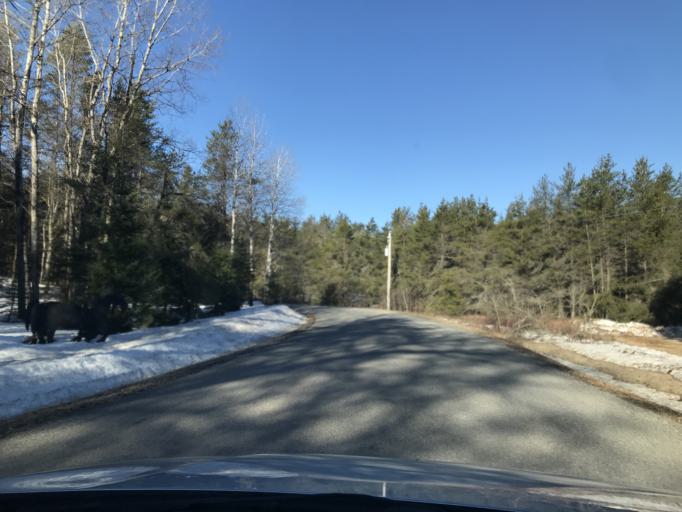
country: US
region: Wisconsin
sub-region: Marinette County
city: Niagara
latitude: 45.3922
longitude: -88.0551
